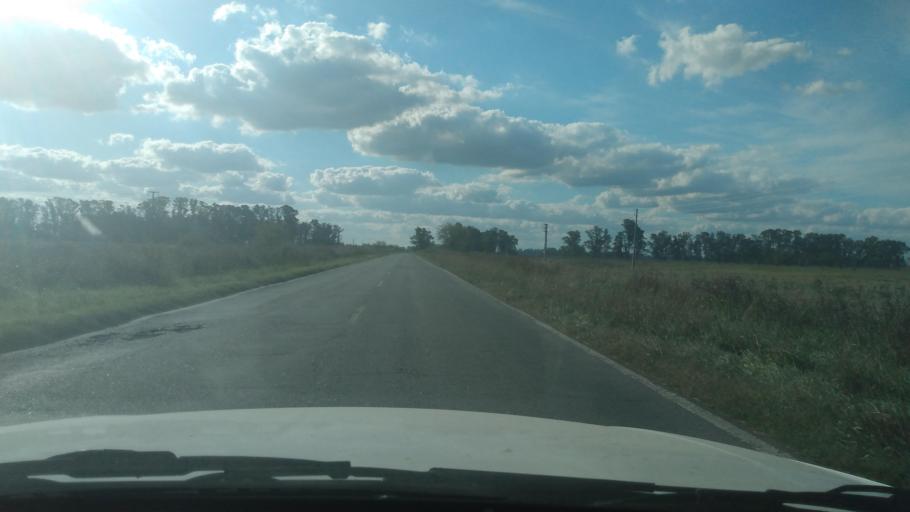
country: AR
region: Buenos Aires
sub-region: Partido de Mercedes
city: Mercedes
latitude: -34.7464
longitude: -59.3827
